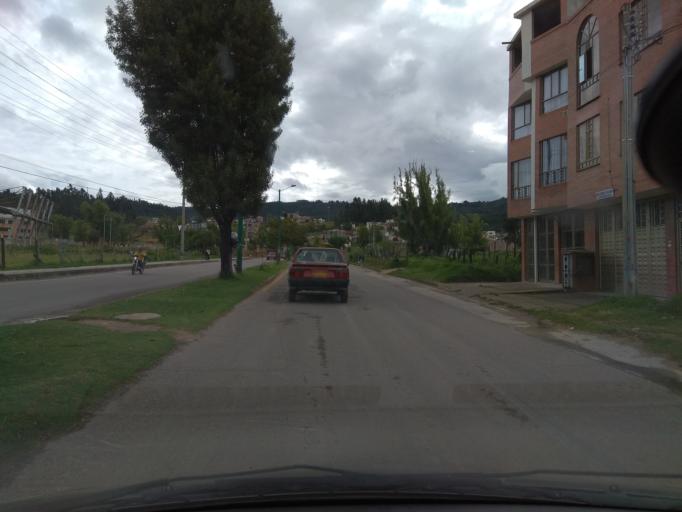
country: CO
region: Boyaca
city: Duitama
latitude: 5.8343
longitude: -73.0281
